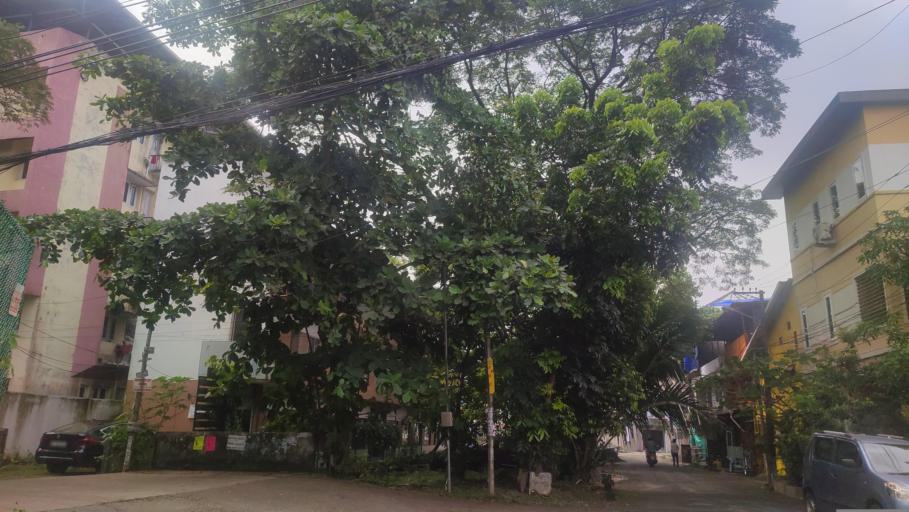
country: IN
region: Kerala
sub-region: Ernakulam
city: Cochin
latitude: 9.9591
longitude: 76.2976
